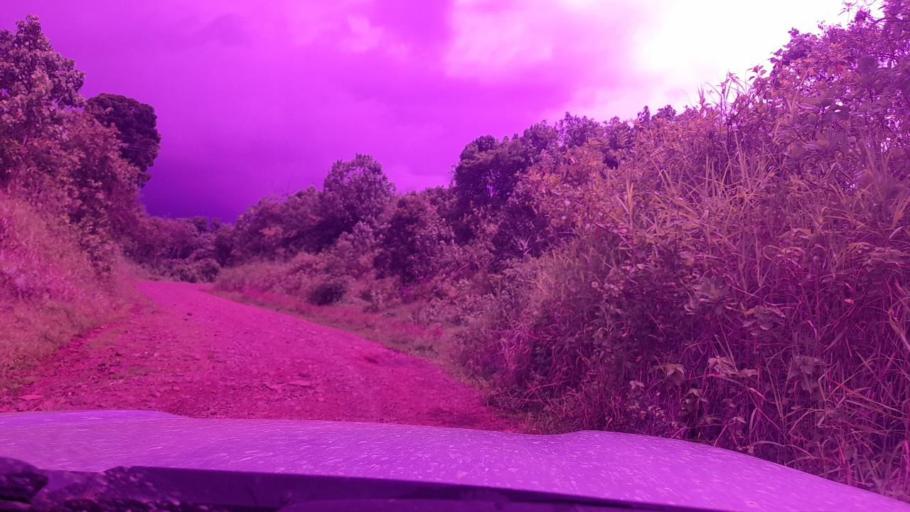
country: ET
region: Southern Nations, Nationalities, and People's Region
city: Tippi
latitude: 7.6278
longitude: 35.5581
